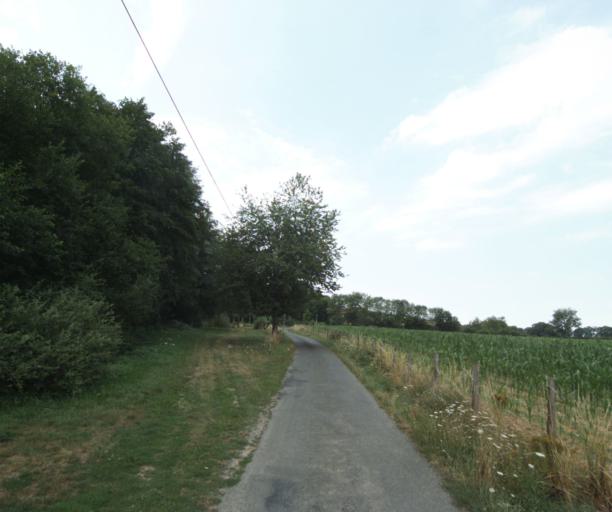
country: FR
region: Bourgogne
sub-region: Departement de Saone-et-Loire
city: Gueugnon
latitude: 46.5891
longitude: 4.0200
